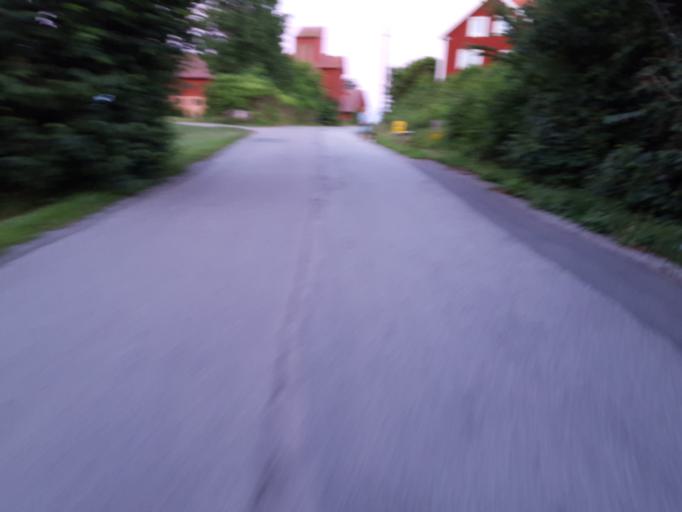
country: SE
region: Uppsala
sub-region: Uppsala Kommun
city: Uppsala
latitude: 59.7838
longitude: 17.5979
